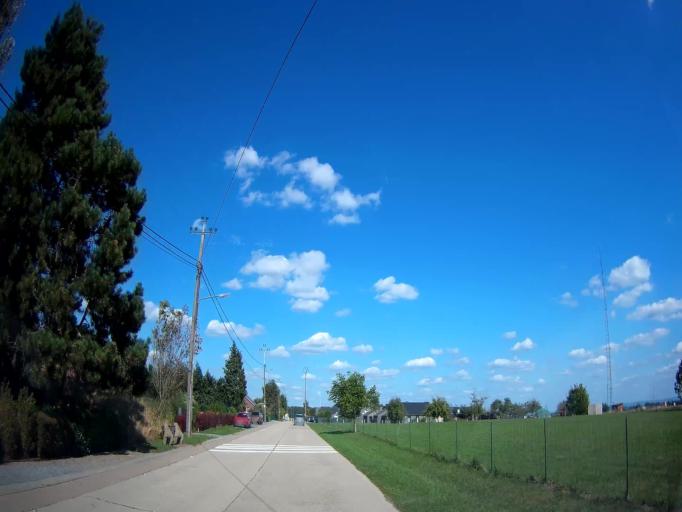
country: FR
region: Champagne-Ardenne
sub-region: Departement des Ardennes
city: Fromelennes
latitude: 50.1689
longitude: 4.8957
